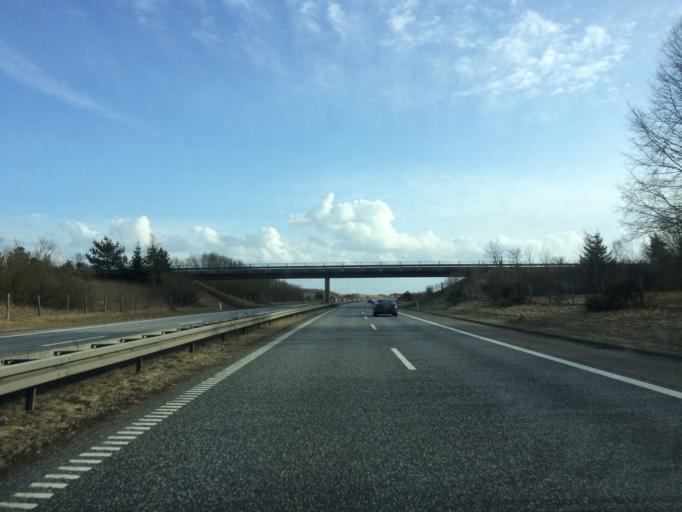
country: DK
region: North Denmark
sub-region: Alborg Kommune
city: Vestbjerg
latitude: 57.1843
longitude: 9.9432
